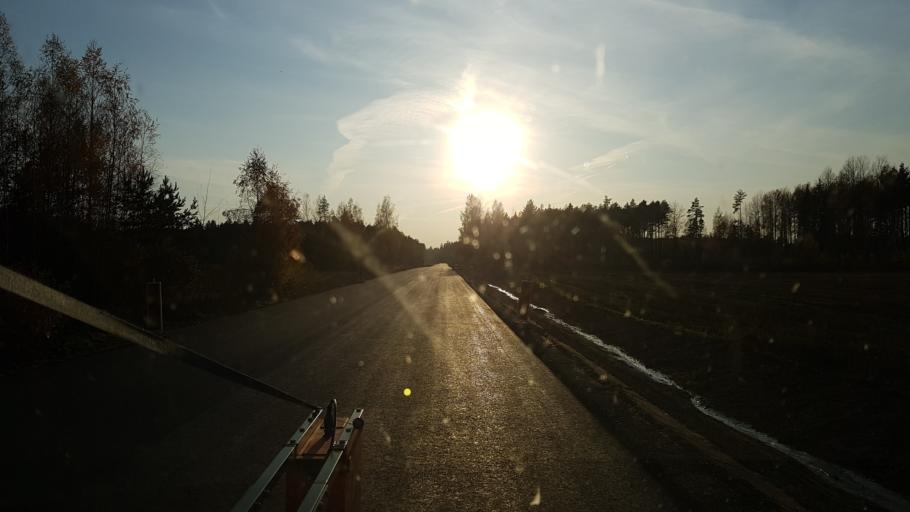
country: EE
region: Polvamaa
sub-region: Polva linn
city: Polva
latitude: 57.9410
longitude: 27.2029
